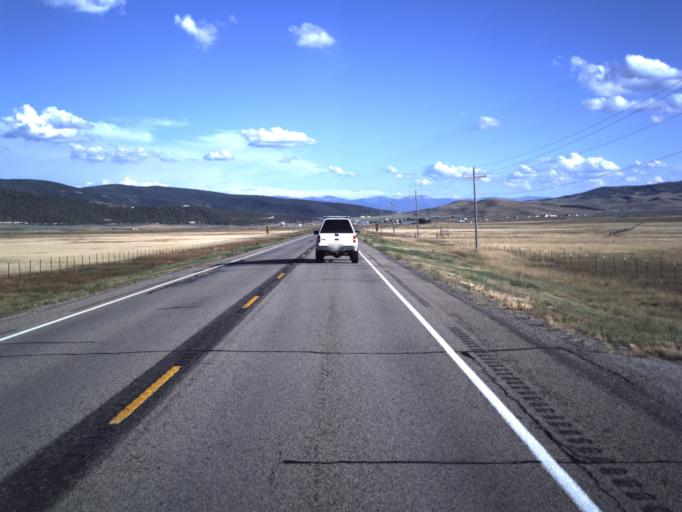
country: US
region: Utah
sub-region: Sanpete County
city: Fairview
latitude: 39.7997
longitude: -111.5009
